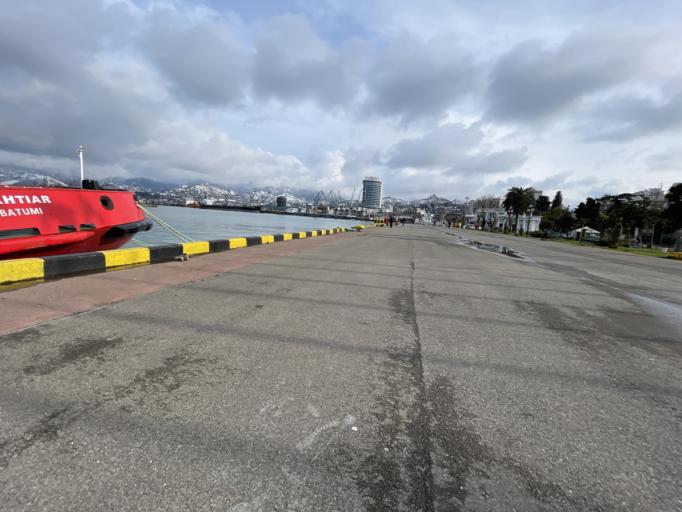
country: GE
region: Ajaria
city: Batumi
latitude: 41.6503
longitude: 41.6448
